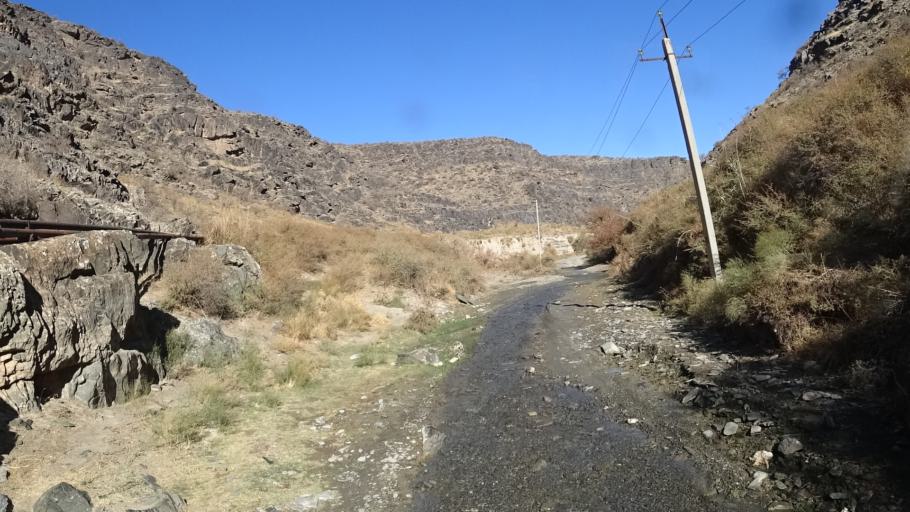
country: UZ
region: Navoiy
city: Nurota
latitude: 40.3076
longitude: 65.6197
